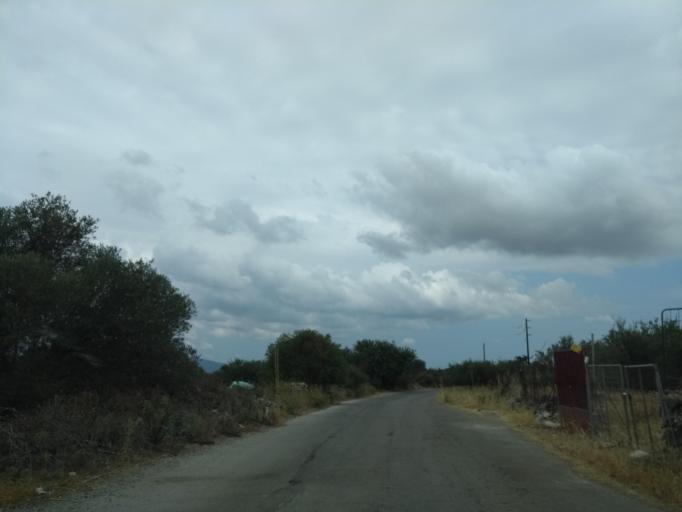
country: GR
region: Crete
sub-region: Nomos Chanias
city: Georgioupolis
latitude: 35.3961
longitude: 24.2299
